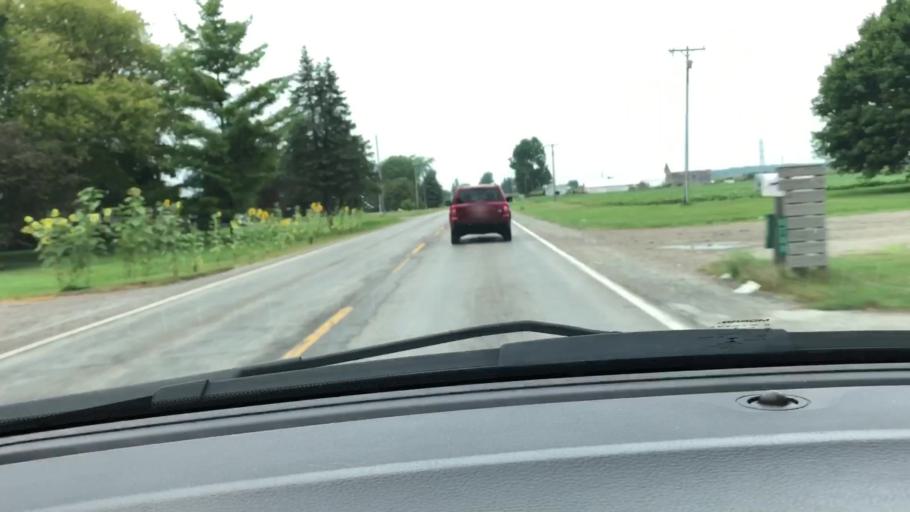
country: US
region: Michigan
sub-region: Saginaw County
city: Freeland
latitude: 43.5507
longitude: -84.0901
